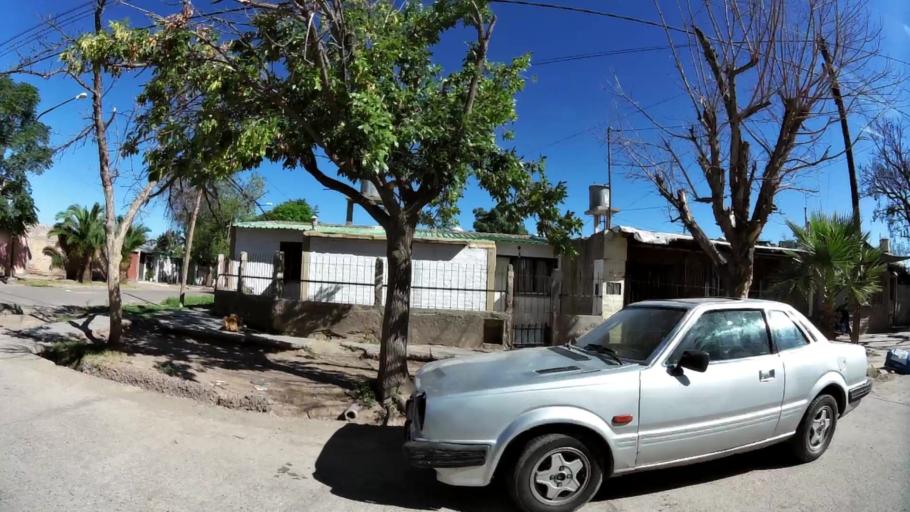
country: AR
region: Mendoza
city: Las Heras
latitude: -32.8386
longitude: -68.8163
